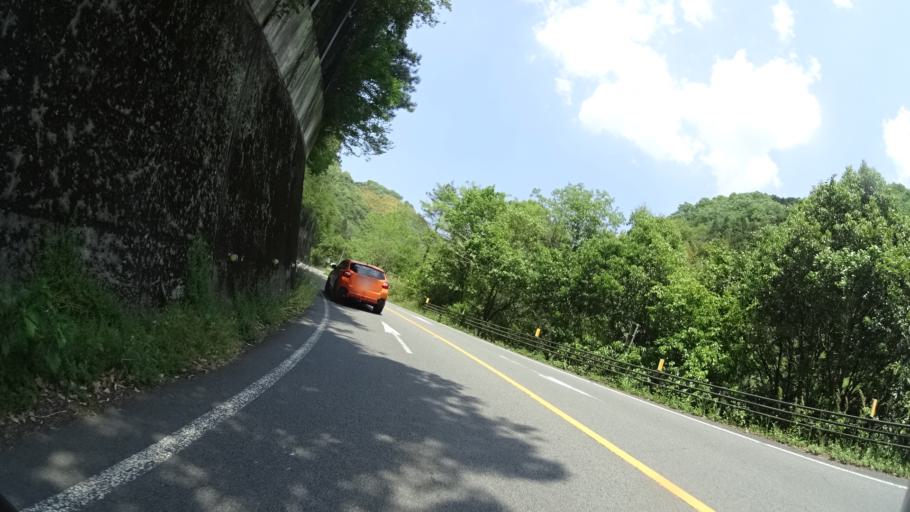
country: JP
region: Ehime
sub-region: Shikoku-chuo Shi
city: Matsuyama
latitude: 33.8930
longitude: 132.8423
